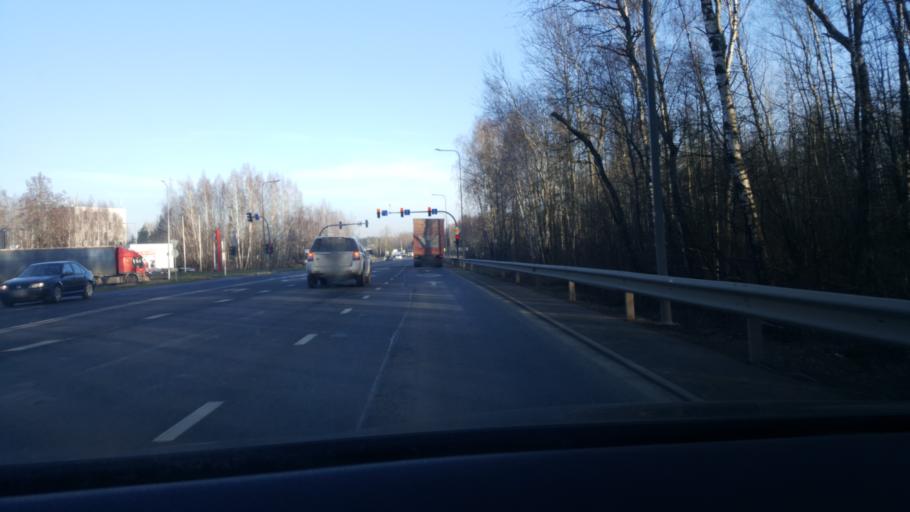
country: LT
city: Ramuciai
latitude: 54.9168
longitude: 24.0394
